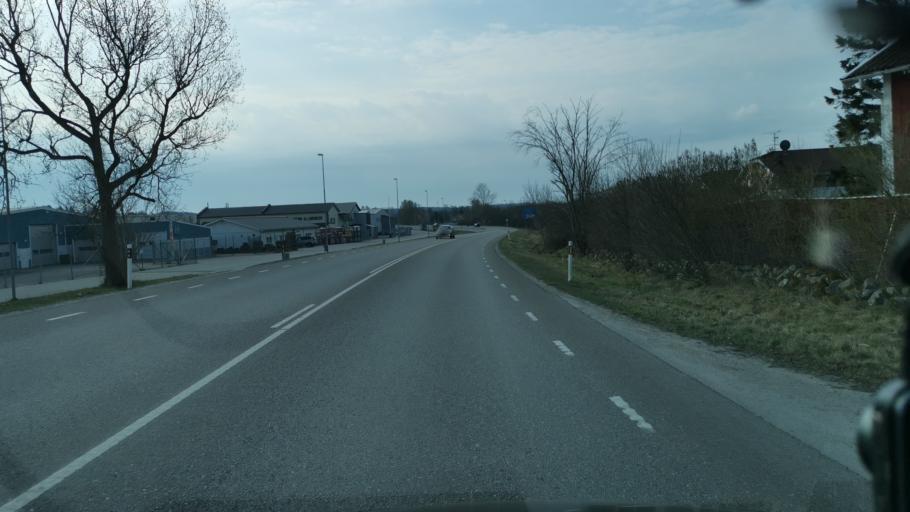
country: SE
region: Vaestra Goetaland
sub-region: Stenungsunds Kommun
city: Stora Hoga
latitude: 57.9906
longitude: 11.8302
